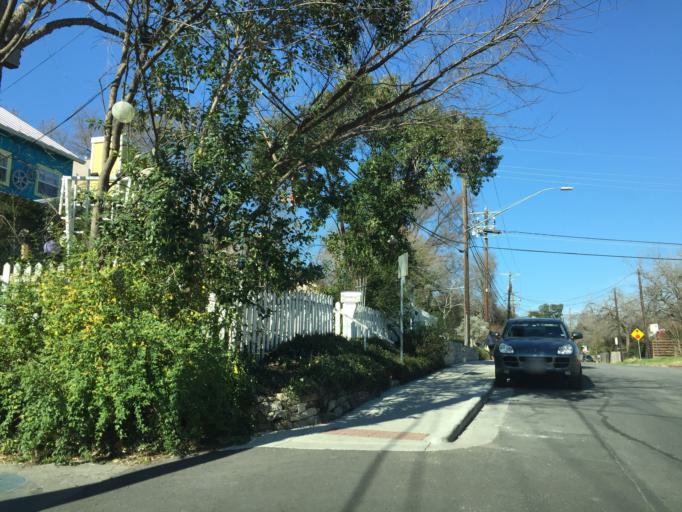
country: US
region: Texas
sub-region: Travis County
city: Austin
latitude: 30.2571
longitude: -97.7636
